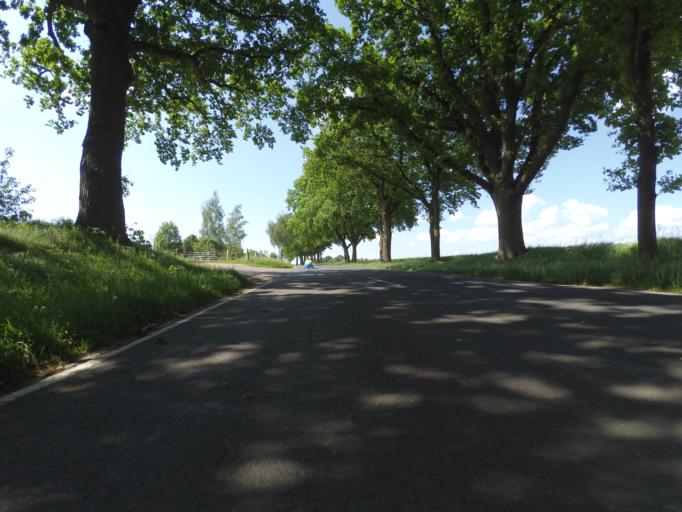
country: DE
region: Lower Saxony
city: Isernhagen Farster Bauerschaft
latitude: 52.5053
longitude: 9.9160
